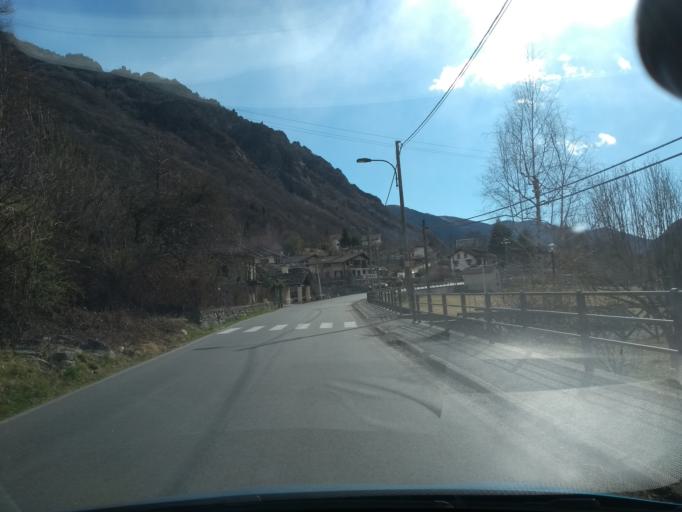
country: IT
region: Piedmont
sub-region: Provincia di Torino
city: Chialamberto
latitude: 45.3621
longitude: 7.3487
